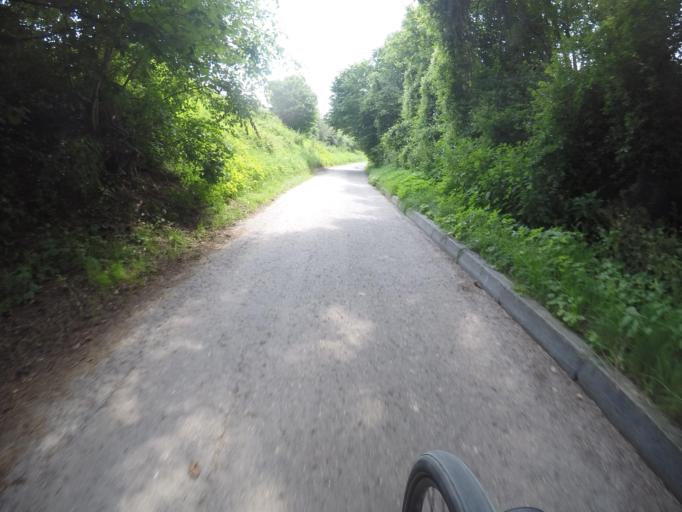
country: DE
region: Baden-Wuerttemberg
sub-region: Freiburg Region
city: Zimmern ob Rottweil
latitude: 48.1756
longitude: 8.6037
